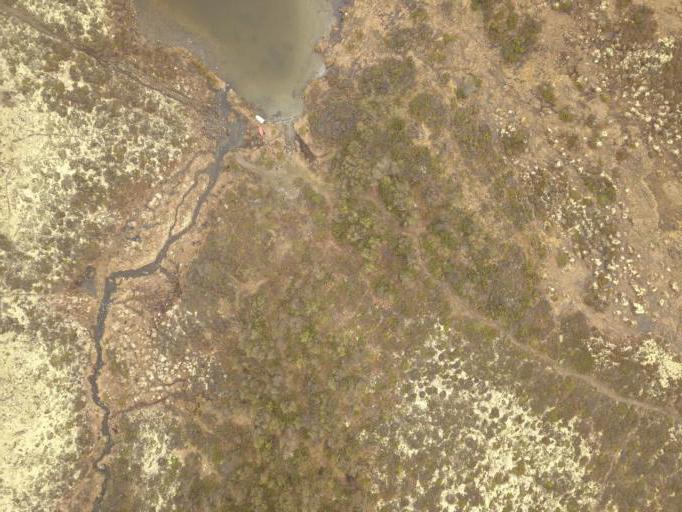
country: NO
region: Hedmark
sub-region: Folldal
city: Folldal
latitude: 62.2307
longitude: 9.6463
